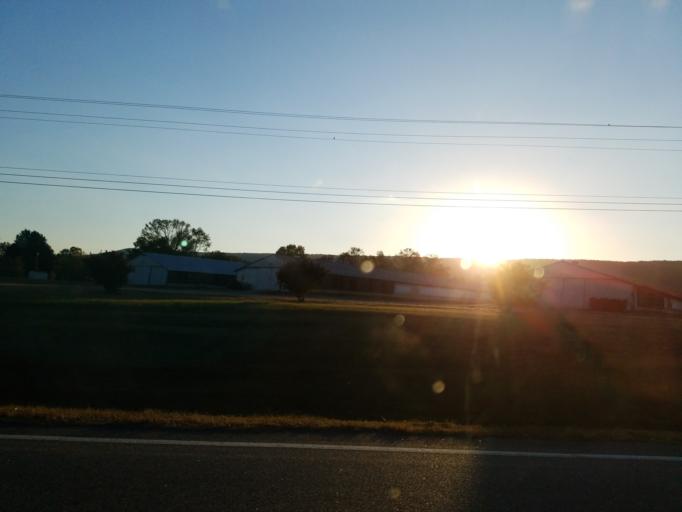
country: US
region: Georgia
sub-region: Gordon County
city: Calhoun
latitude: 34.5883
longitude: -85.0352
